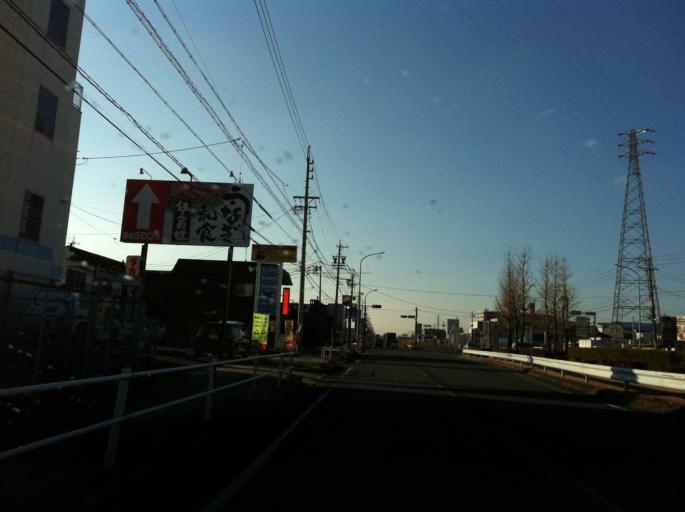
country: JP
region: Aichi
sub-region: Tokai-shi
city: Toyokawa
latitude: 34.8293
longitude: 137.4079
